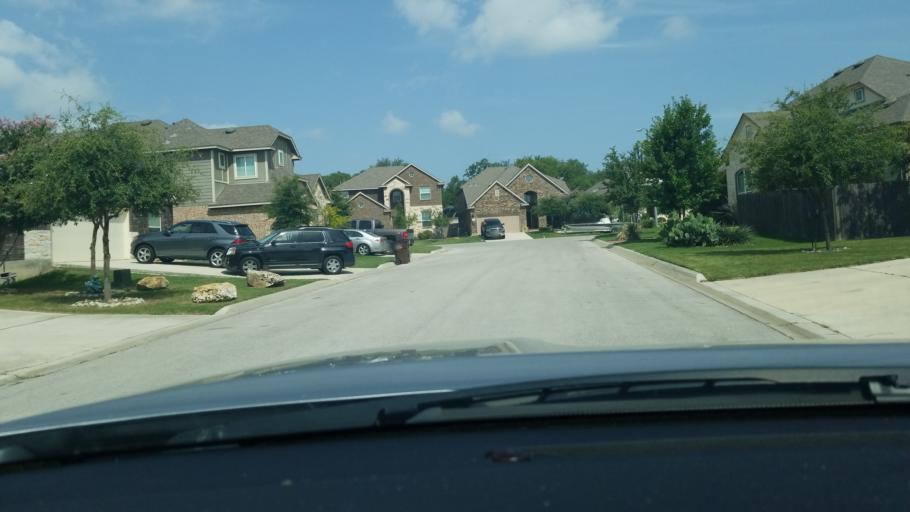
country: US
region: Texas
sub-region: Bexar County
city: Timberwood Park
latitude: 29.6912
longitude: -98.4927
